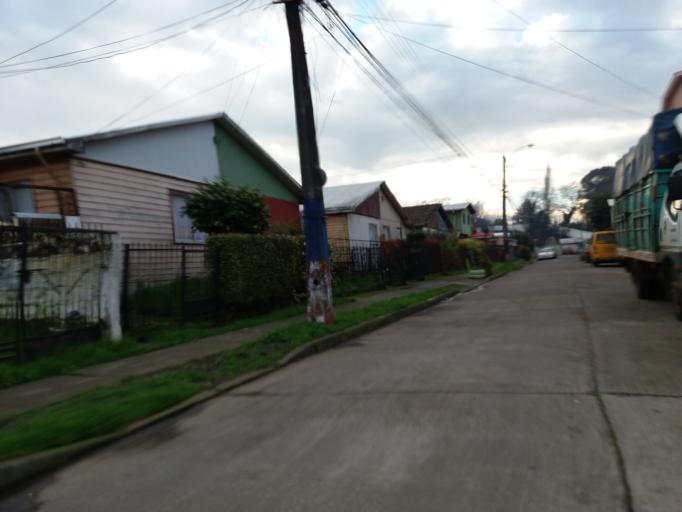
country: CL
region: Araucania
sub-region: Provincia de Cautin
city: Temuco
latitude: -38.7478
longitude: -72.6054
